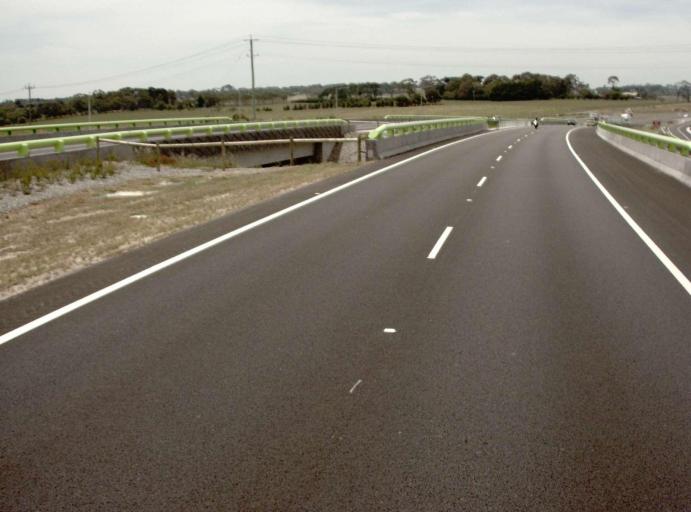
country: AU
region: Victoria
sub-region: Mornington Peninsula
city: Mount Martha
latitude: -38.2709
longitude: 145.0702
